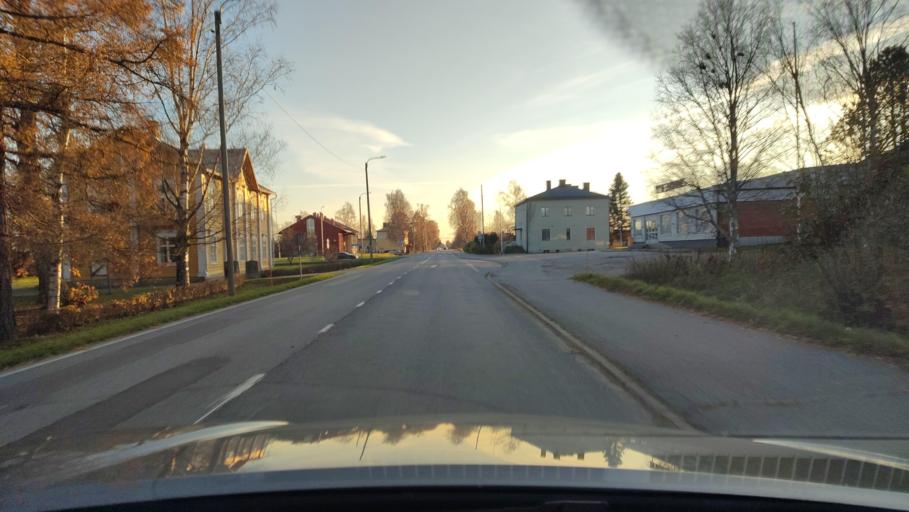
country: FI
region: Ostrobothnia
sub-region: Sydosterbotten
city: Naerpes
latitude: 62.5449
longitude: 21.3964
